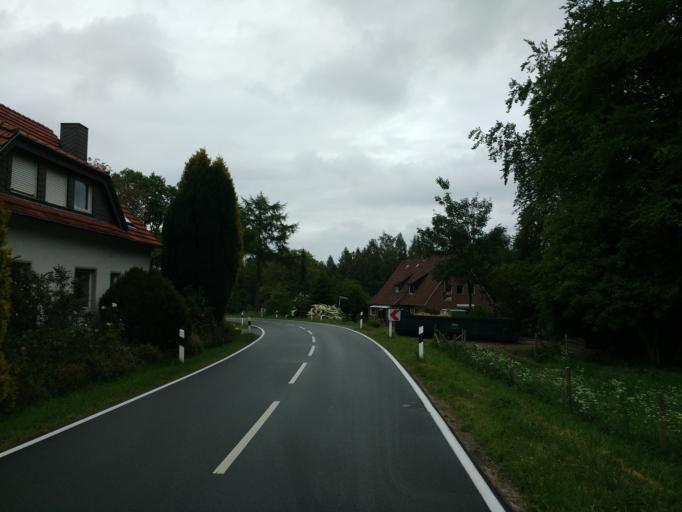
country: DE
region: Lower Saxony
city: Bad Iburg
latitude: 52.1740
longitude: 8.0724
